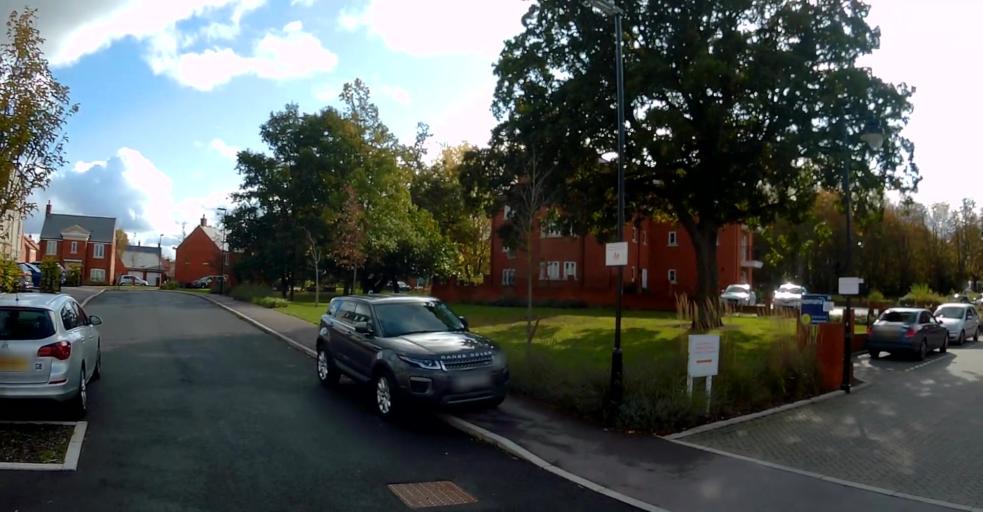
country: GB
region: England
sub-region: Hampshire
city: Aldershot
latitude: 51.2552
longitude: -0.7636
